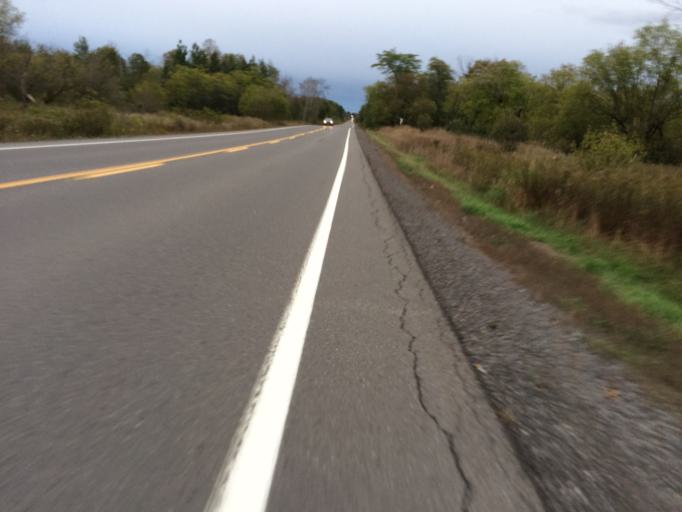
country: CA
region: Ontario
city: Ottawa
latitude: 45.3064
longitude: -75.6434
